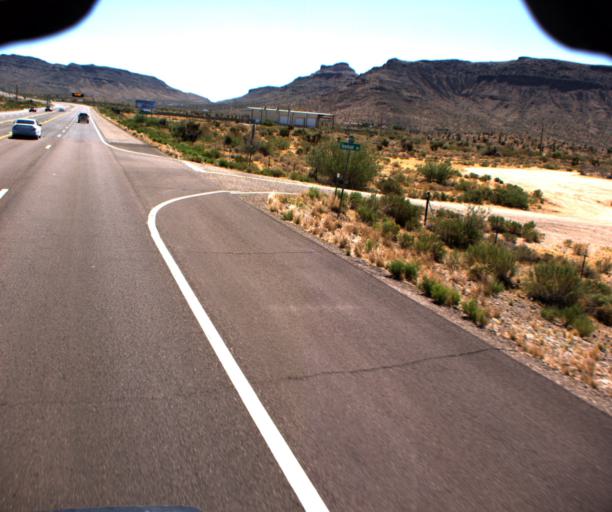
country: US
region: Arizona
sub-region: Mohave County
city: Golden Valley
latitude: 35.2186
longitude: -114.1480
